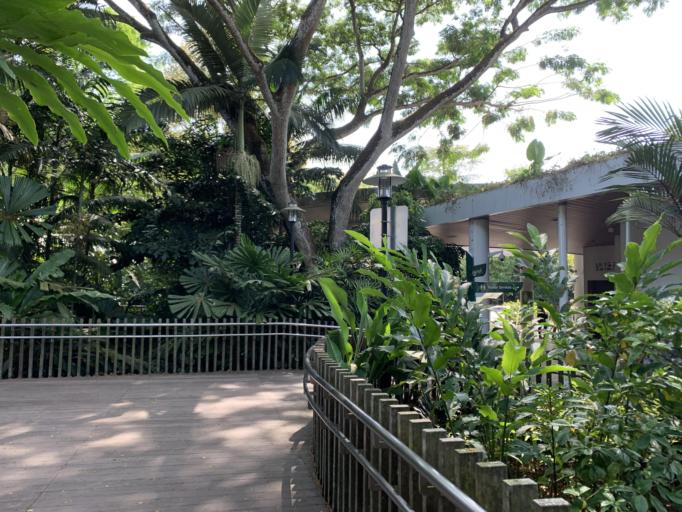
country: SG
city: Singapore
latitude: 1.3209
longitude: 103.8176
